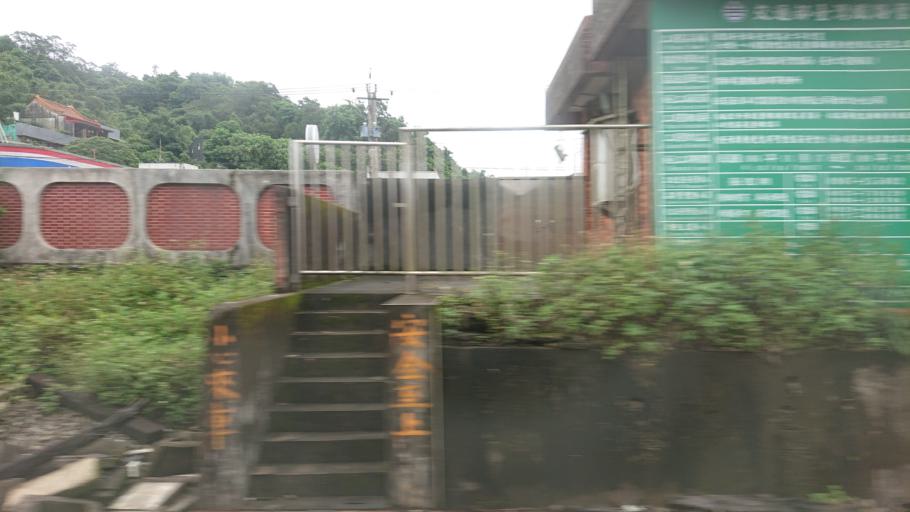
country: TW
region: Taiwan
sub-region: Keelung
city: Keelung
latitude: 25.1058
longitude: 121.7261
